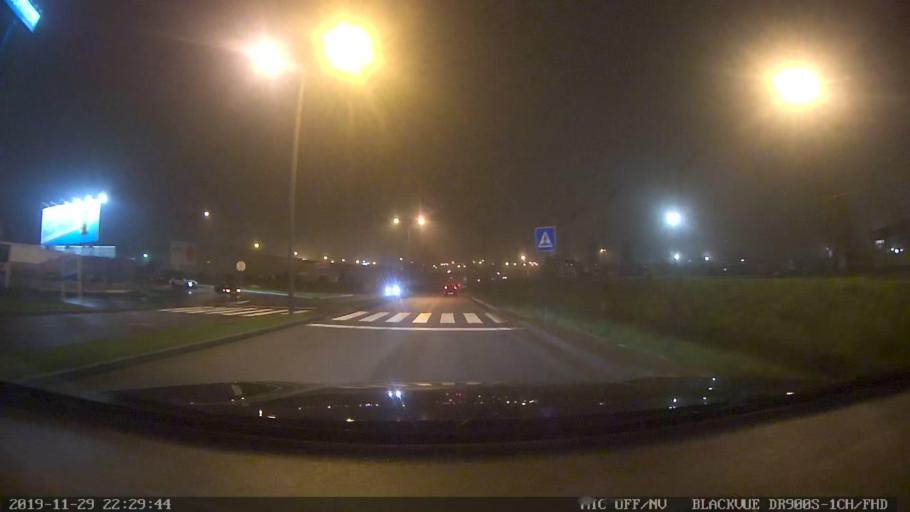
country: PT
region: Porto
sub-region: Matosinhos
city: Santa Cruz do Bispo
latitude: 41.2176
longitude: -8.6840
